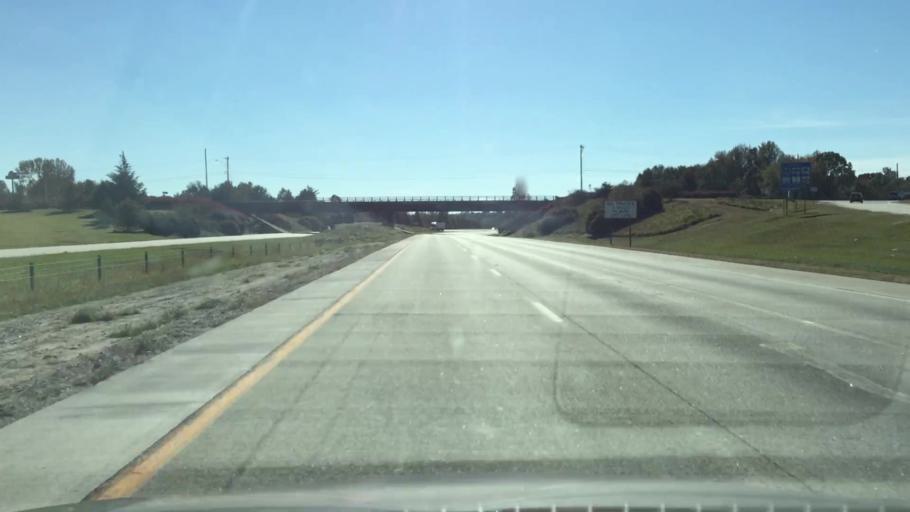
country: US
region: North Carolina
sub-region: Randolph County
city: Archdale
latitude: 35.9055
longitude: -79.9531
